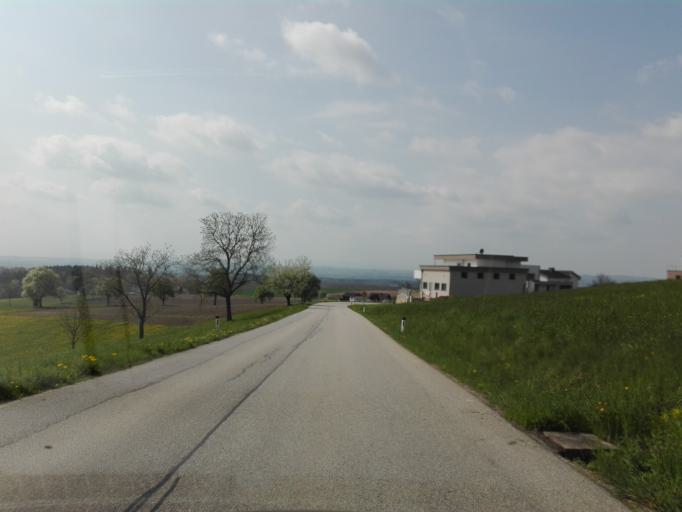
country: AT
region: Upper Austria
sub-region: Politischer Bezirk Perg
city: Perg
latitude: 48.2442
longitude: 14.7010
